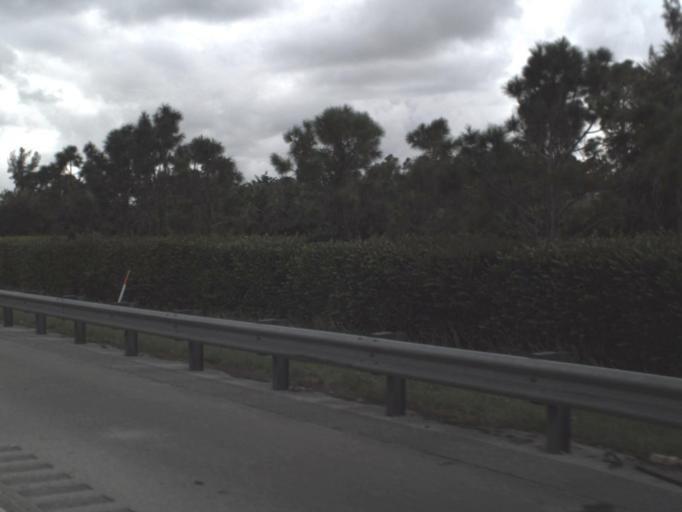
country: US
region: Florida
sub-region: Palm Beach County
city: Greenacres City
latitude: 26.6281
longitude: -80.1743
